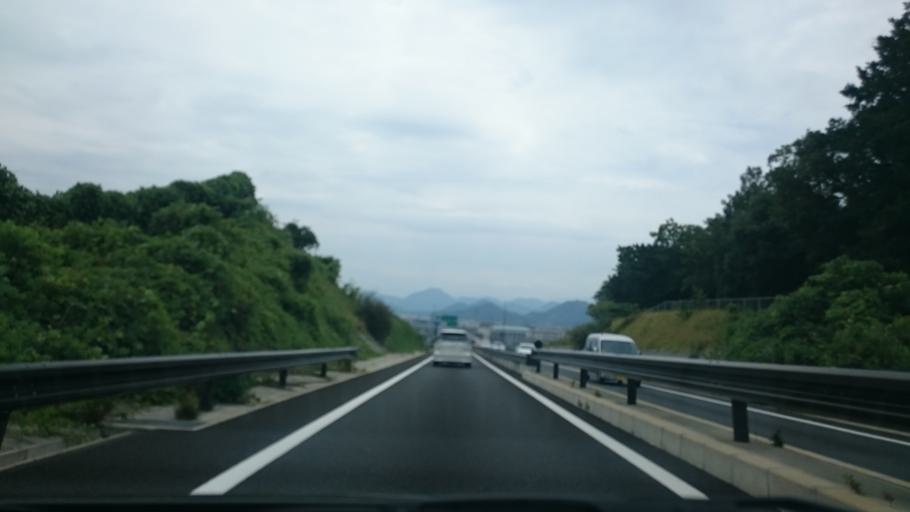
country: JP
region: Shizuoka
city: Mishima
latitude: 35.1011
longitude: 138.9482
